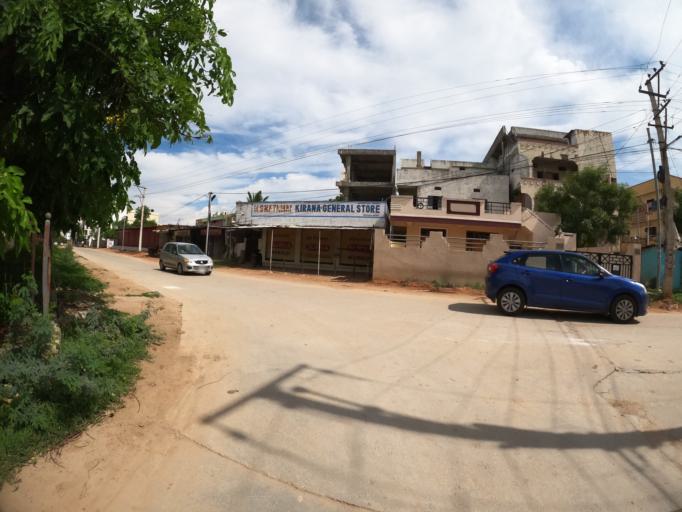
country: IN
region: Telangana
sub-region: Hyderabad
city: Hyderabad
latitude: 17.3598
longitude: 78.3793
